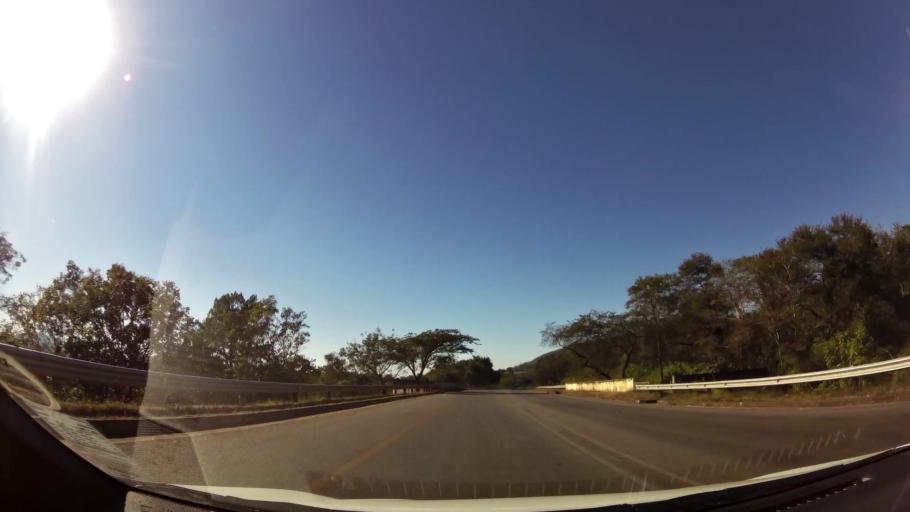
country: ZA
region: Limpopo
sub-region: Mopani District Municipality
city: Tzaneen
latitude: -23.8382
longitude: 30.1869
